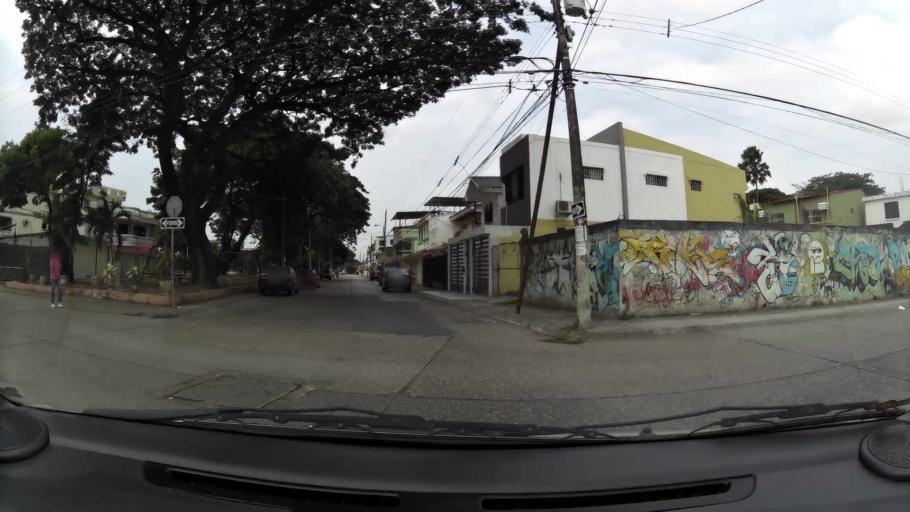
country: EC
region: Guayas
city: Eloy Alfaro
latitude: -2.1202
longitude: -79.8959
